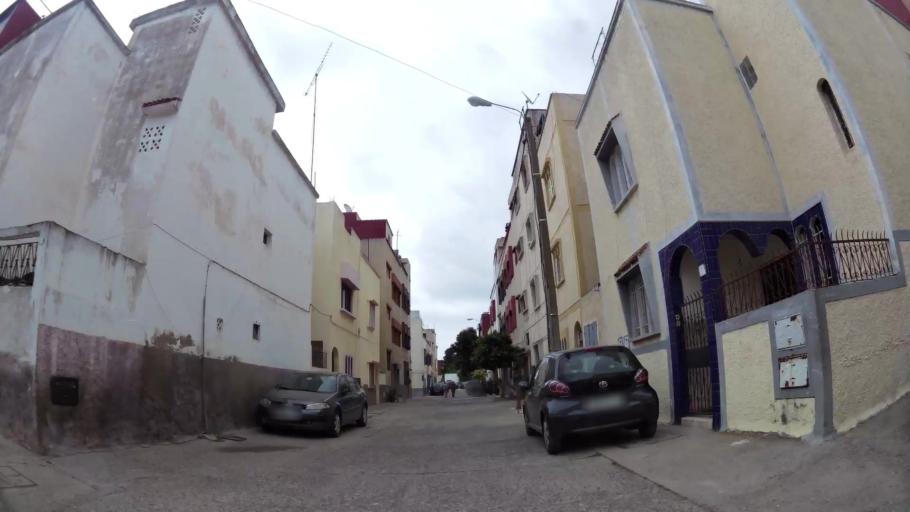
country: MA
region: Rabat-Sale-Zemmour-Zaer
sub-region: Rabat
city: Rabat
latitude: 33.9782
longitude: -6.8221
